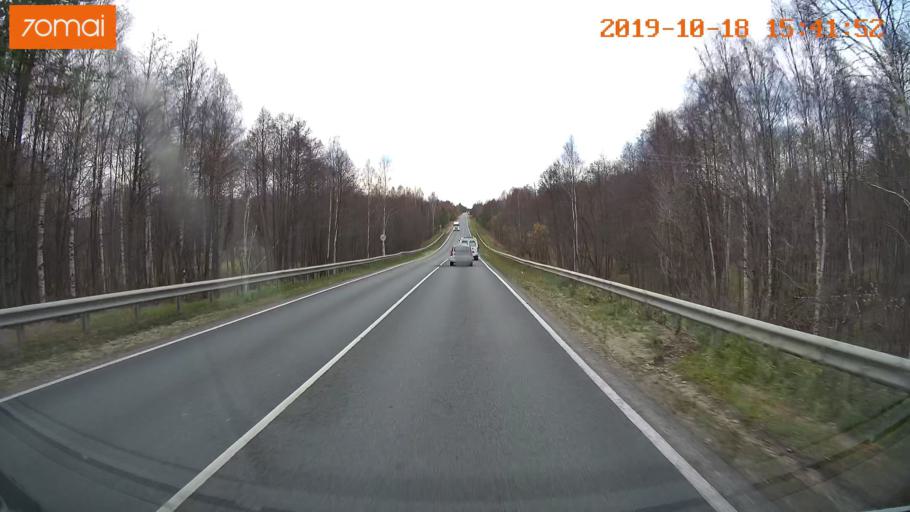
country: RU
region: Vladimir
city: Golovino
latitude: 55.9499
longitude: 40.5766
